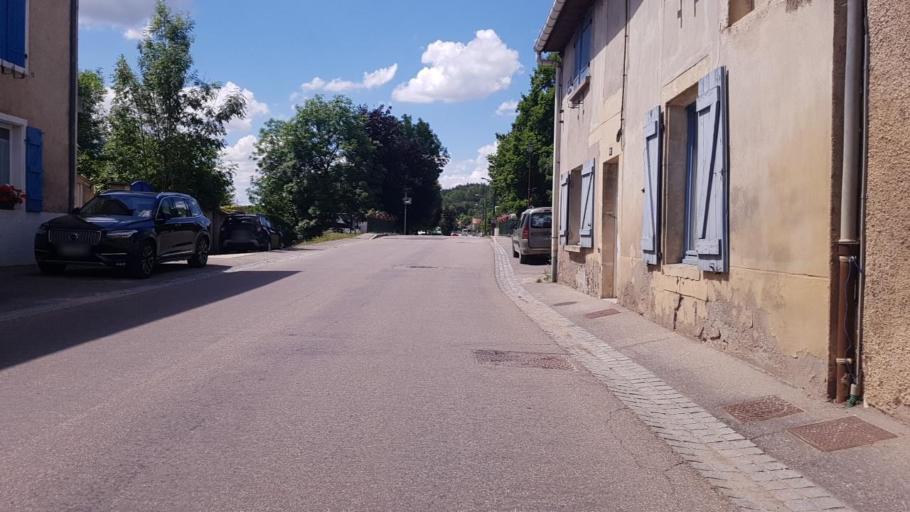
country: FR
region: Lorraine
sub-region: Departement de la Meuse
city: Vacon
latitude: 48.6858
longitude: 5.6165
